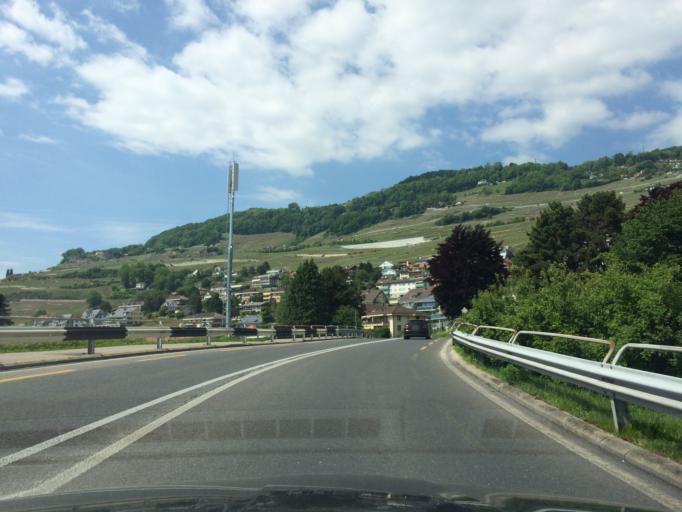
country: CH
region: Vaud
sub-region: Riviera-Pays-d'Enhaut District
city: Chardonne
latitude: 46.4687
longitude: 6.8232
